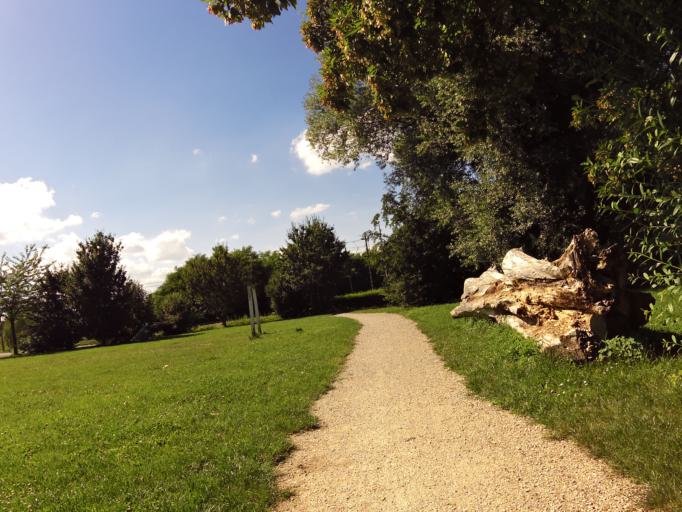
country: DE
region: Baden-Wuerttemberg
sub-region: Freiburg Region
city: Radolfzell am Bodensee
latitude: 47.7391
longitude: 8.9796
